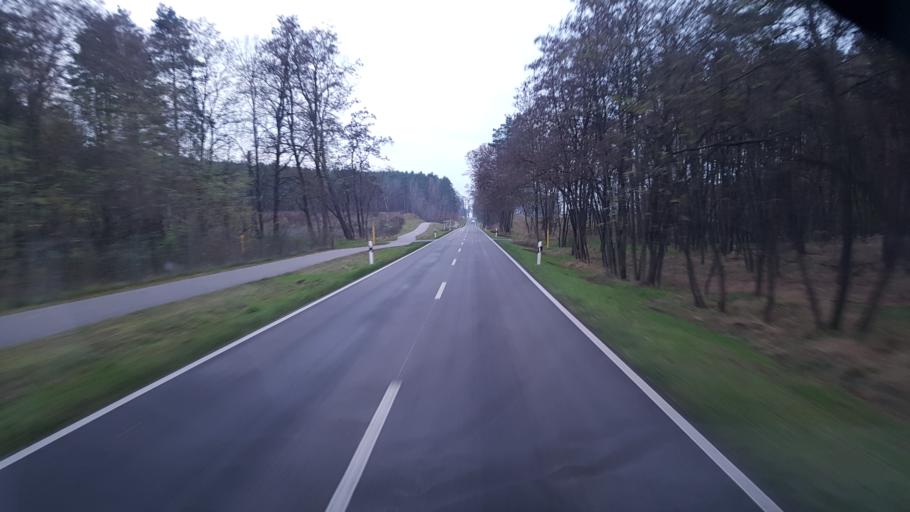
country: DE
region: Brandenburg
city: Gross Lindow
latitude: 52.1336
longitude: 14.5226
